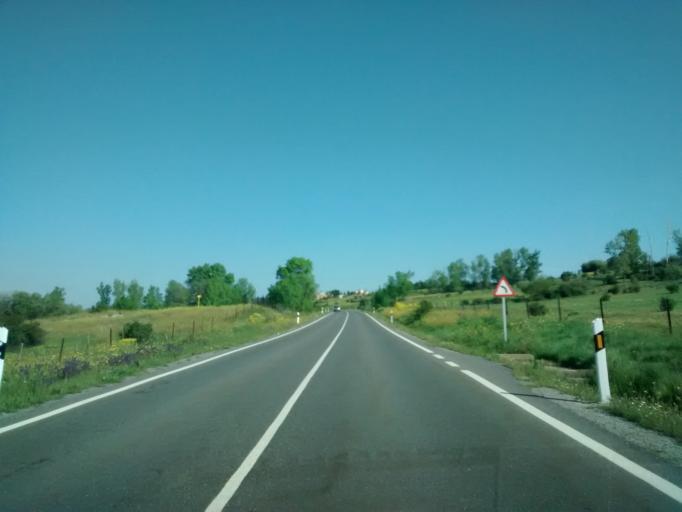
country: ES
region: Castille and Leon
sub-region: Provincia de Segovia
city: San Ildefonso
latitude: 40.9190
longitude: -4.0204
